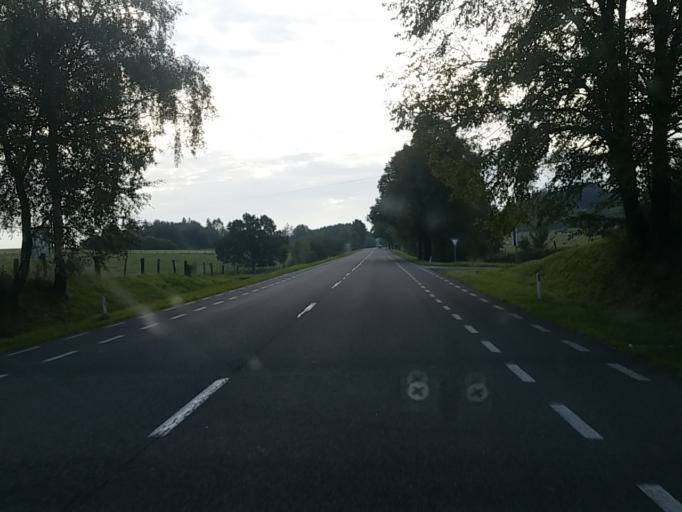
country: BE
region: Wallonia
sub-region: Province du Luxembourg
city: Herbeumont
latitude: 49.7220
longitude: 5.2441
